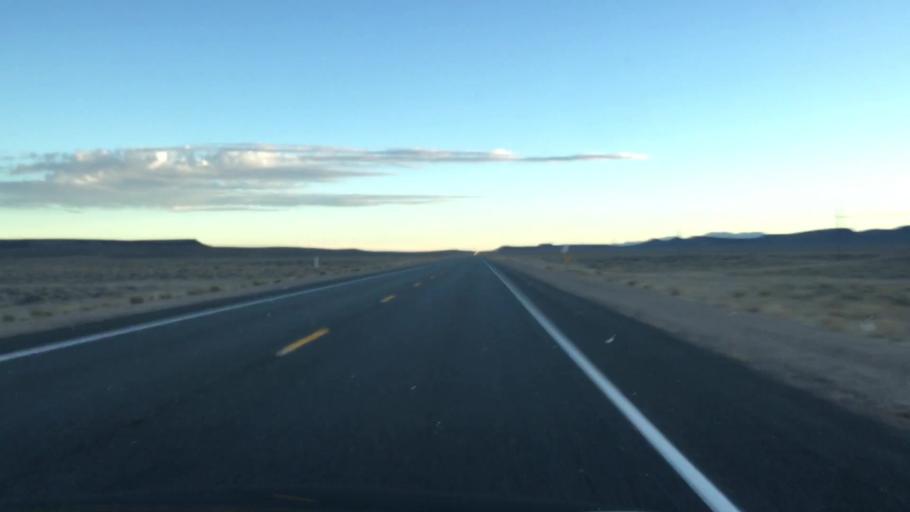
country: US
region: Nevada
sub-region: Esmeralda County
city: Goldfield
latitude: 37.4421
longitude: -117.1652
